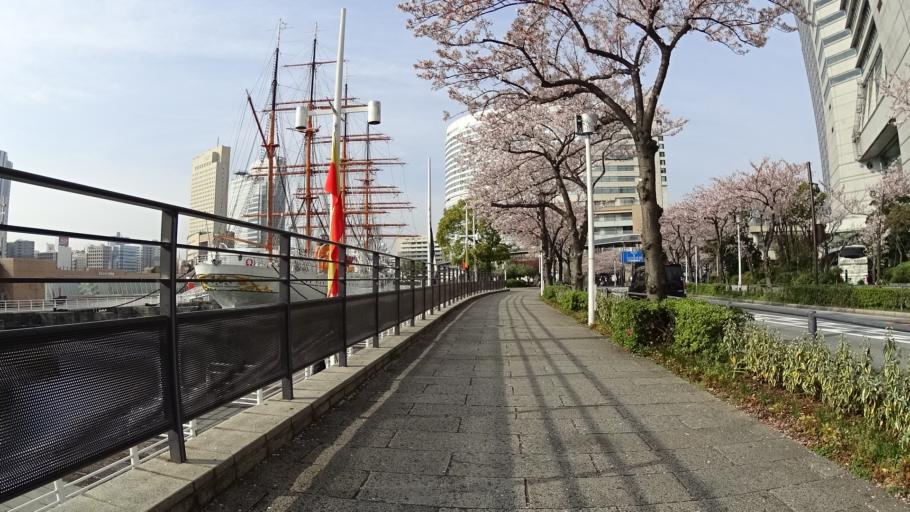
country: JP
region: Kanagawa
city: Yokohama
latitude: 35.4546
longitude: 139.6326
